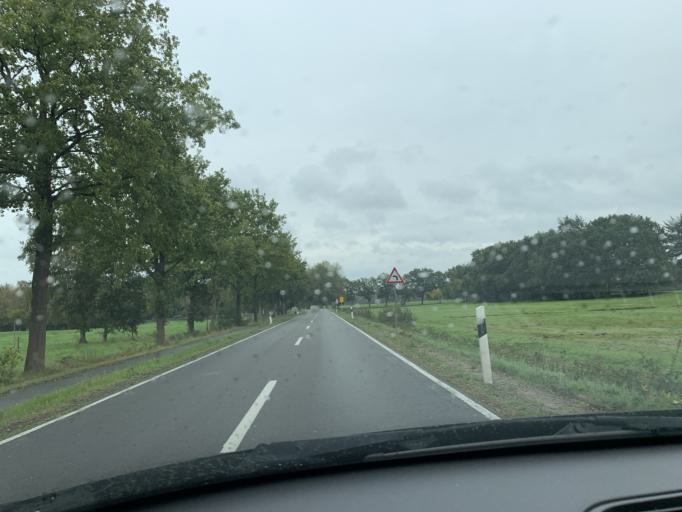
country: DE
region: Lower Saxony
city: Bad Zwischenahn
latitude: 53.1539
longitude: 8.0886
